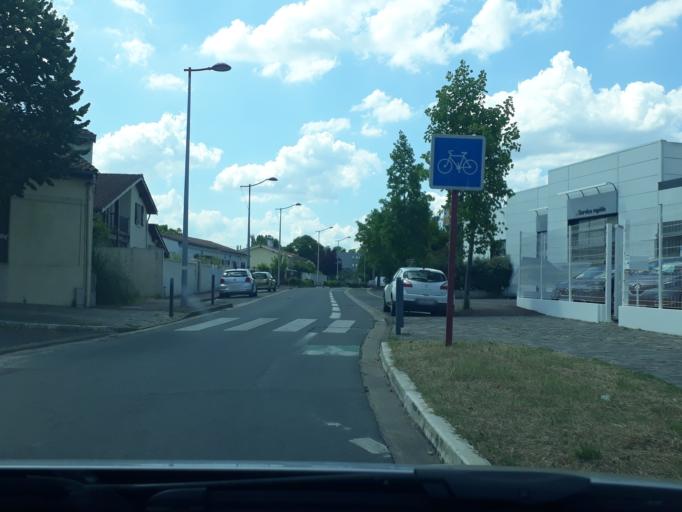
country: FR
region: Aquitaine
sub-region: Departement de la Gironde
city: Le Haillan
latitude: 44.8419
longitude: -0.6676
